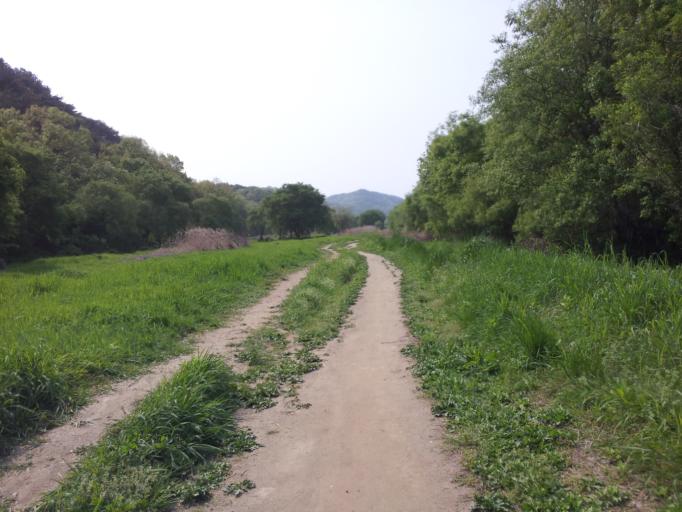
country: KR
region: Daejeon
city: Daejeon
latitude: 36.3394
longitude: 127.3536
